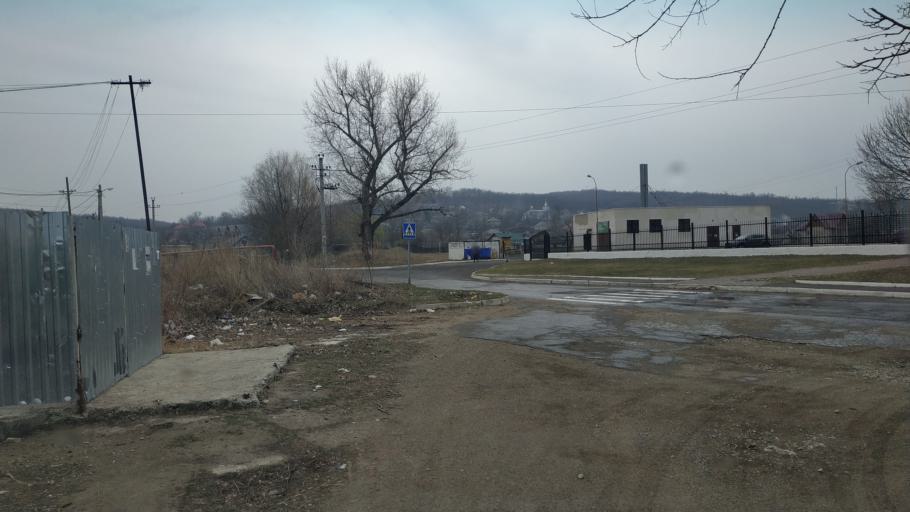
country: MD
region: Chisinau
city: Singera
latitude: 46.9144
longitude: 28.9754
